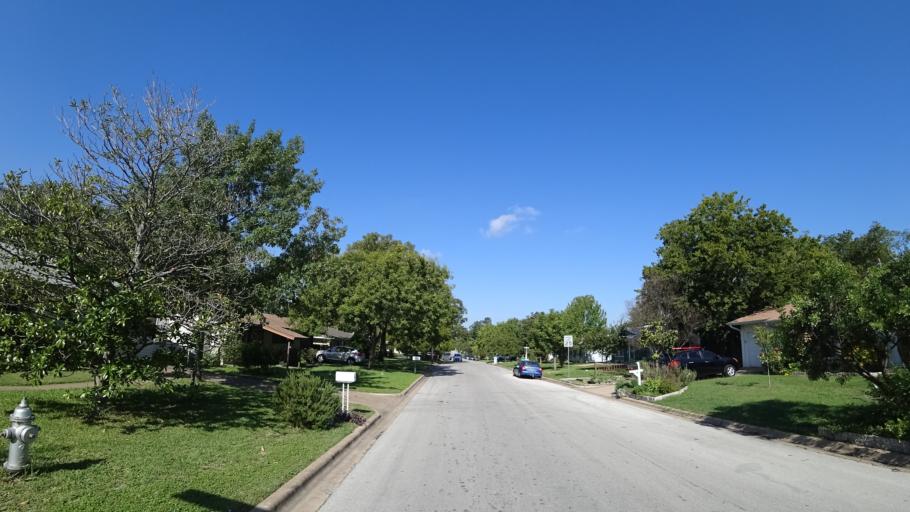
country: US
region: Texas
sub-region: Travis County
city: Austin
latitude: 30.3379
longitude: -97.7083
